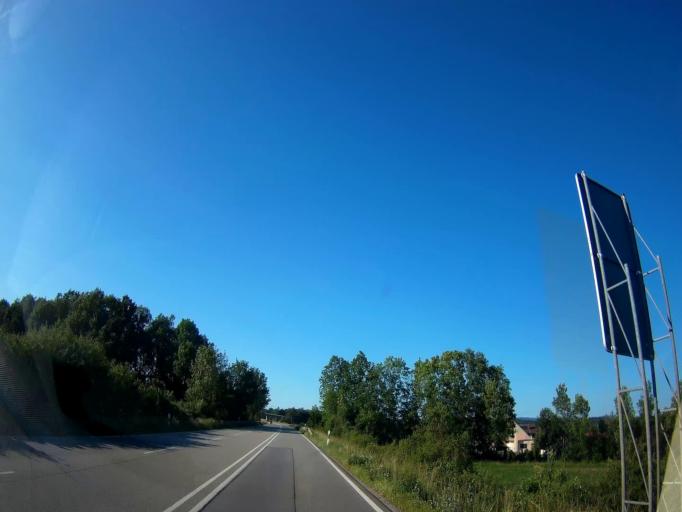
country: DE
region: Bavaria
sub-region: Lower Bavaria
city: Steinach
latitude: 48.9296
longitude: 12.6218
